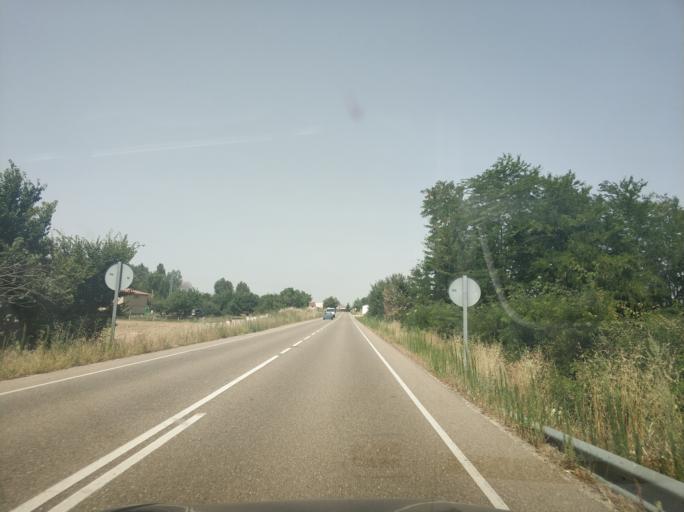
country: ES
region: Castille and Leon
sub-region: Provincia de Salamanca
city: Valverdon
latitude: 41.0447
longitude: -5.7631
